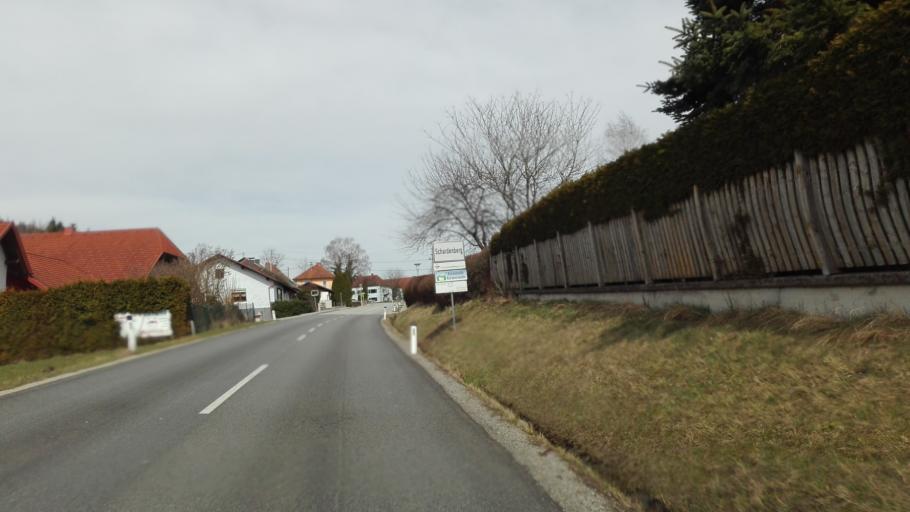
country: DE
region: Bavaria
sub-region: Lower Bavaria
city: Passau
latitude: 48.5159
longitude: 13.4930
